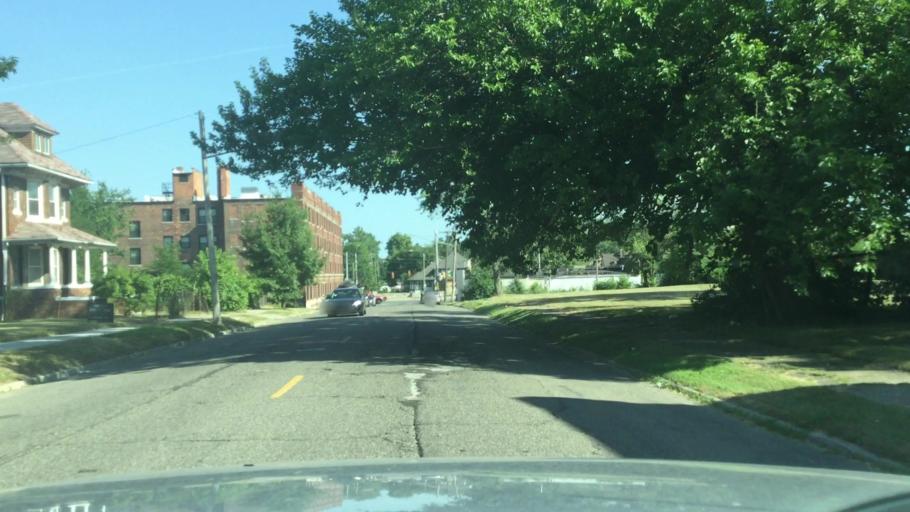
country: US
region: Michigan
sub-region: Wayne County
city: Grosse Pointe Park
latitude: 42.3603
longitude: -82.9857
